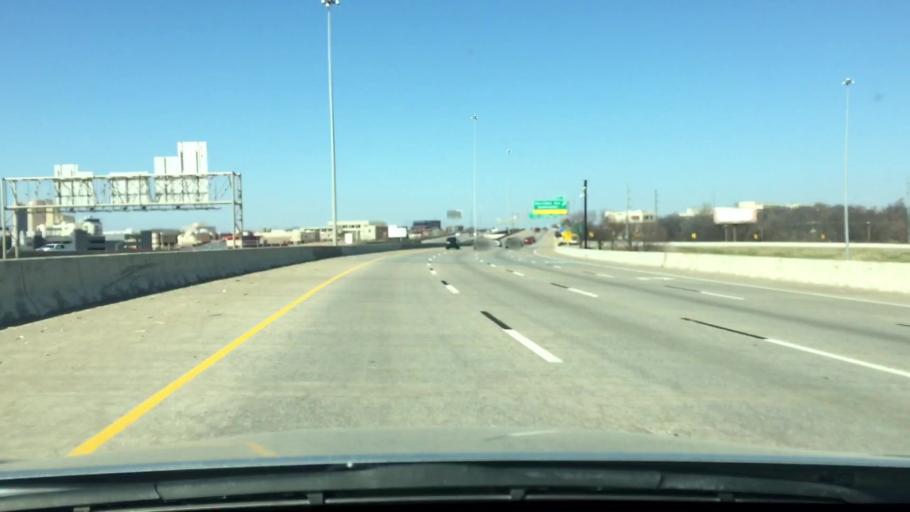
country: US
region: Oklahoma
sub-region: Oklahoma County
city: Oklahoma City
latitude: 35.4654
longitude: -97.4992
